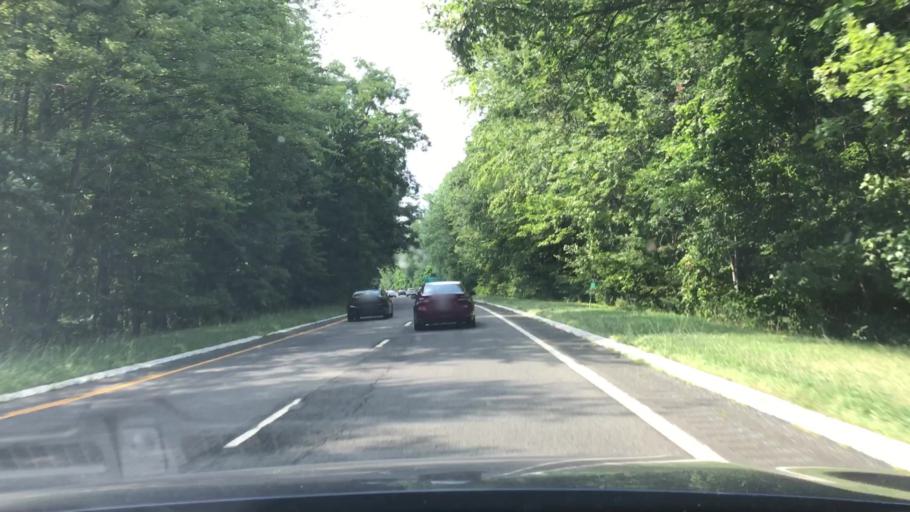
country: US
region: New York
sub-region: Rockland County
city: Bardonia
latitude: 41.1157
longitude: -74.0026
